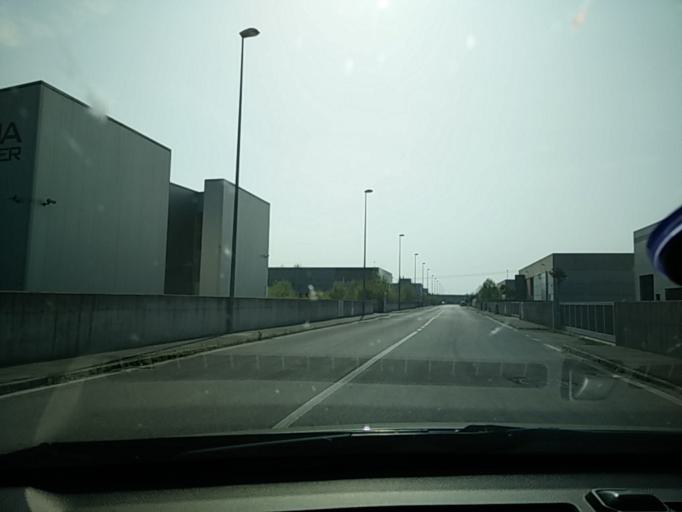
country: IT
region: Friuli Venezia Giulia
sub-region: Provincia di Pordenone
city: Fiume Veneto
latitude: 45.9515
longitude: 12.7216
